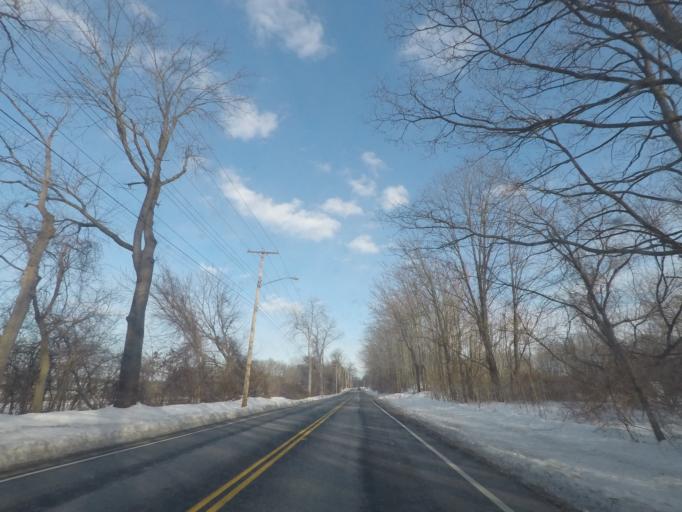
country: US
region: New York
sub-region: Schenectady County
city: Schenectady
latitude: 42.8307
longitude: -73.9436
